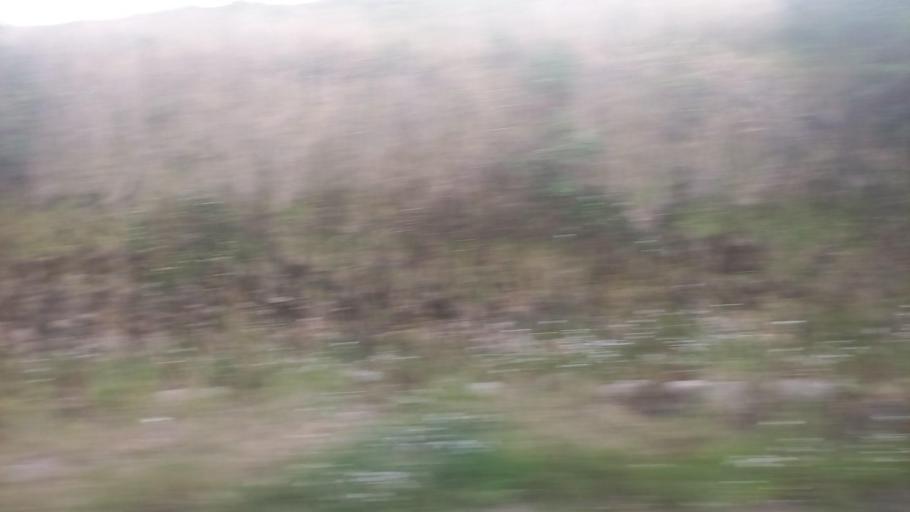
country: EC
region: Pichincha
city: Cayambe
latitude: 0.0784
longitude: -78.1085
